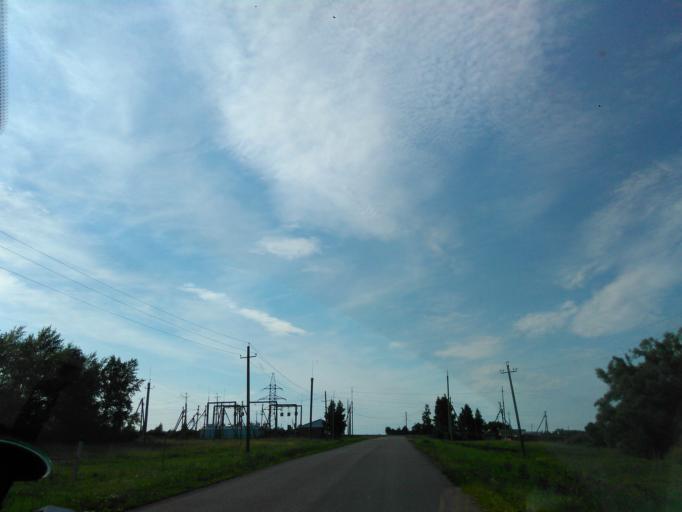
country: RU
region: Penza
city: Lermontovo
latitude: 52.9903
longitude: 43.6446
